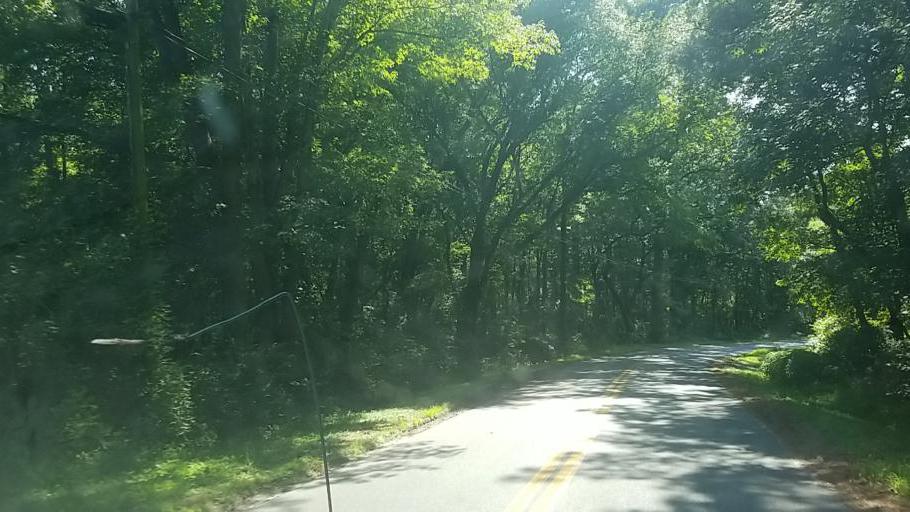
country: US
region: Maryland
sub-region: Somerset County
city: Princess Anne
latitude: 38.2601
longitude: -75.6695
